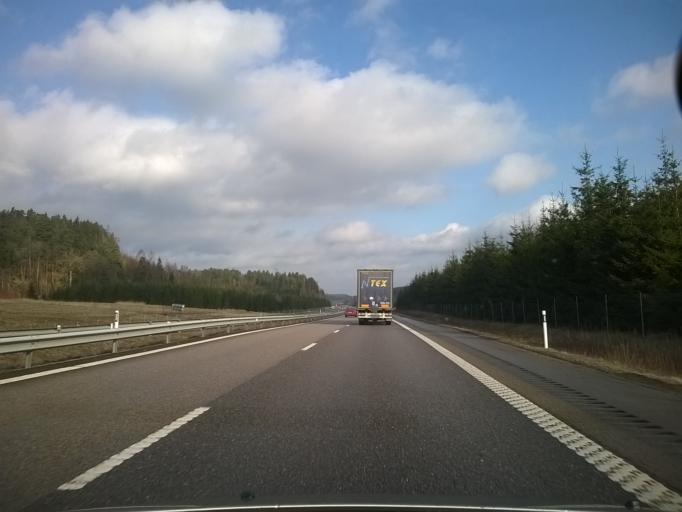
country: SE
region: Vaestra Goetaland
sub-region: Uddevalla Kommun
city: Ljungskile
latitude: 58.2640
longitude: 11.8963
